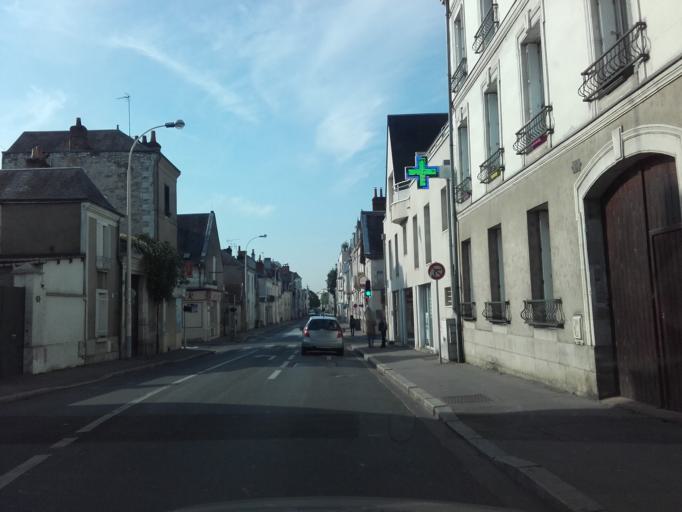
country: FR
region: Centre
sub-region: Departement d'Indre-et-Loire
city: La Riche
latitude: 47.3931
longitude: 0.6721
